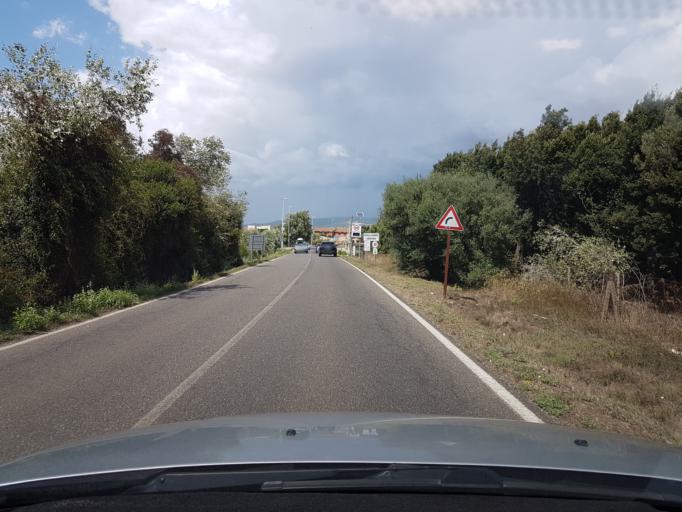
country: IT
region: Sardinia
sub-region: Provincia di Oristano
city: Riola Sardo
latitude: 39.9871
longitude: 8.5405
